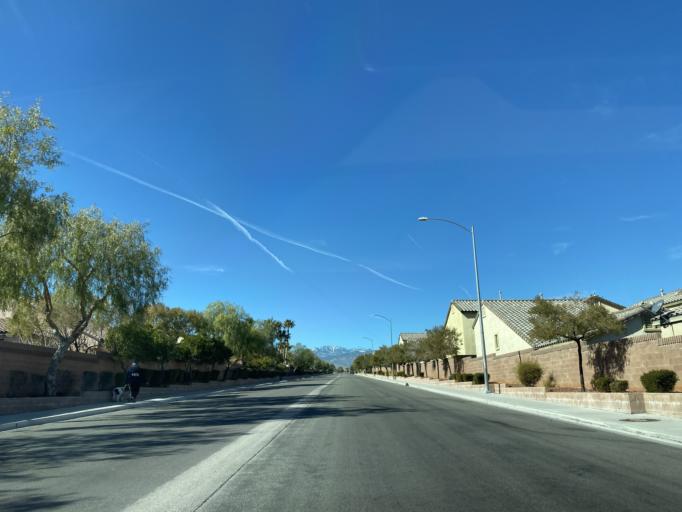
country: US
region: Nevada
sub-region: Clark County
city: Summerlin South
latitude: 36.3030
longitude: -115.3070
